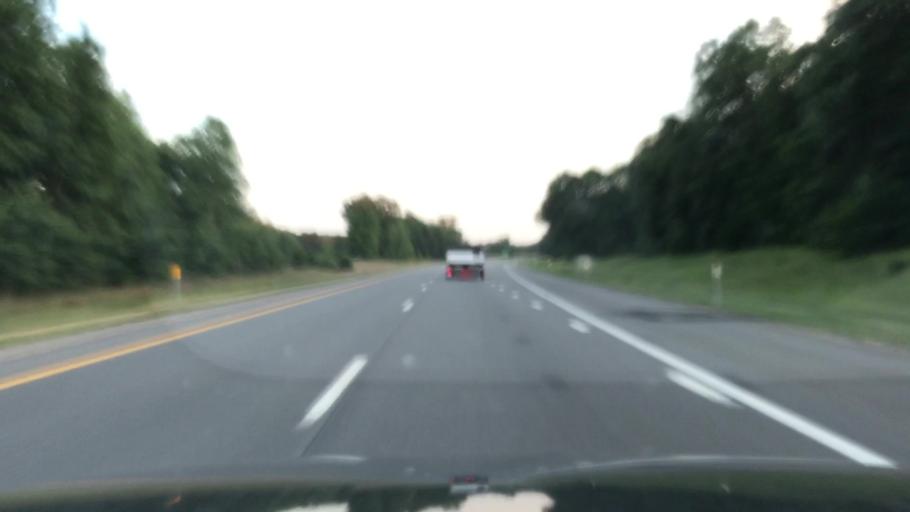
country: US
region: Michigan
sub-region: Montcalm County
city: Howard City
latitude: 43.4326
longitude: -85.4941
